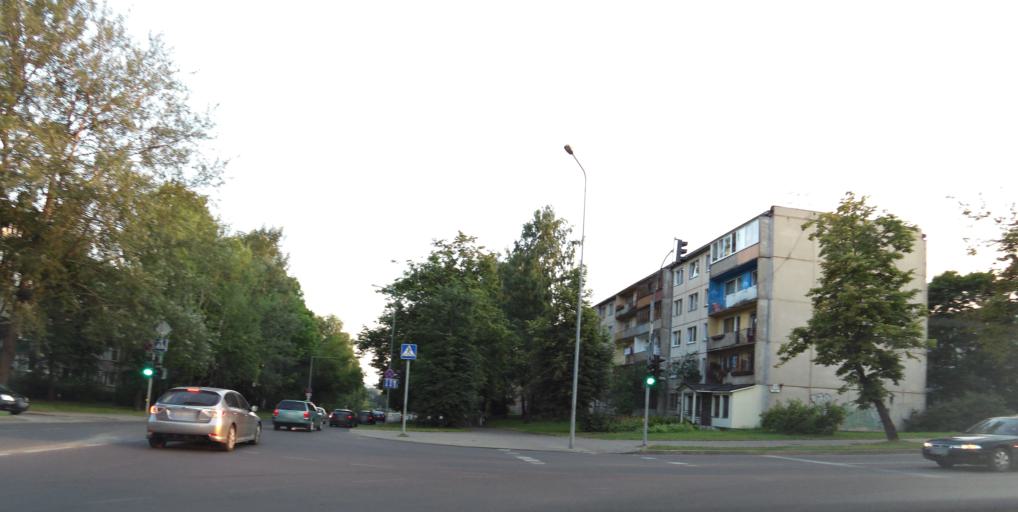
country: LT
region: Vilnius County
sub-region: Vilnius
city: Vilnius
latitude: 54.7076
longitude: 25.2906
